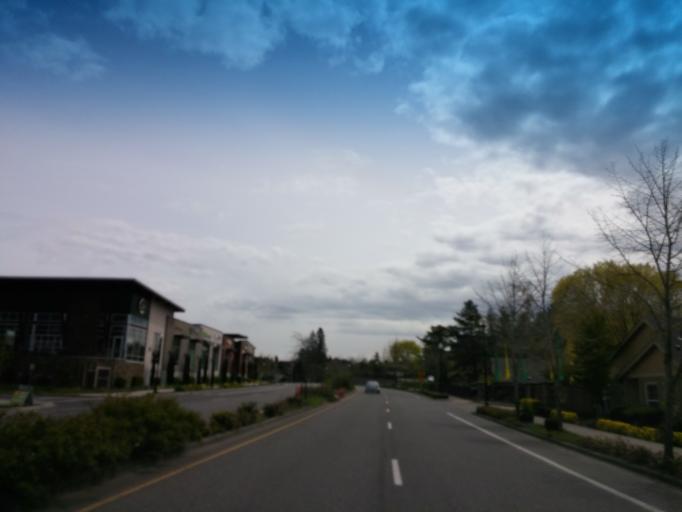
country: US
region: Oregon
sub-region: Washington County
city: Cedar Mill
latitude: 45.5213
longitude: -122.8041
